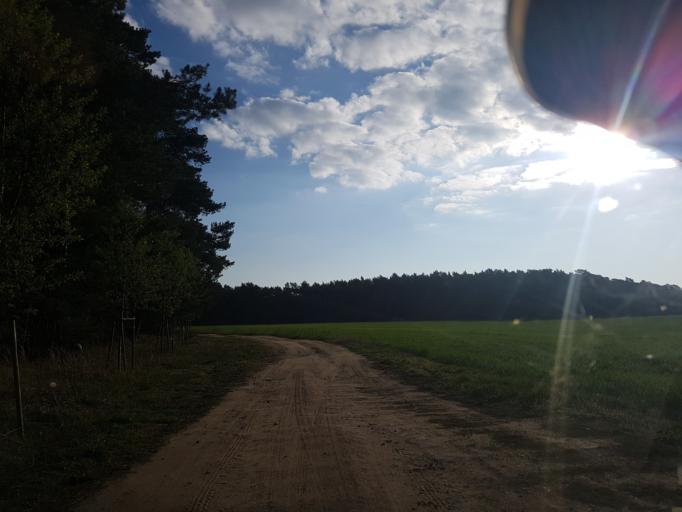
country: DE
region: Brandenburg
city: Treuenbrietzen
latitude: 52.1096
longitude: 12.8332
